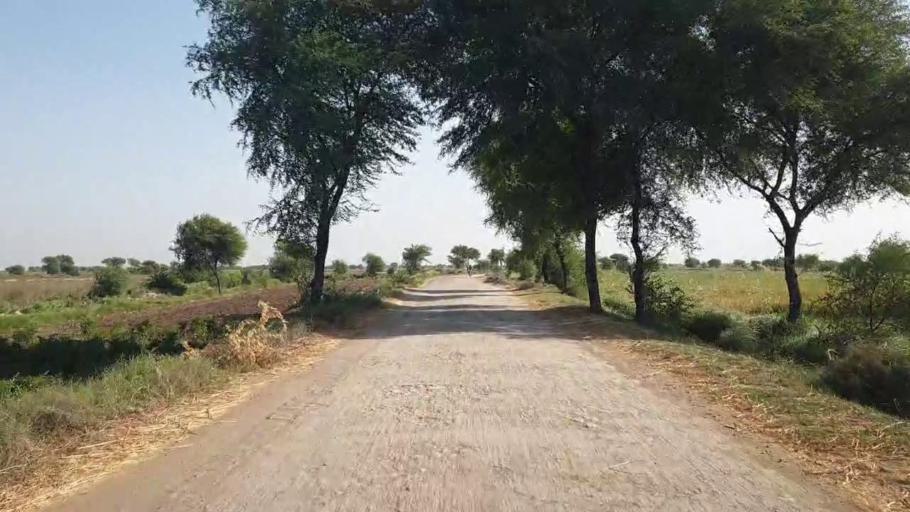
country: PK
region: Sindh
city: Matli
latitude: 25.0518
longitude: 68.7224
